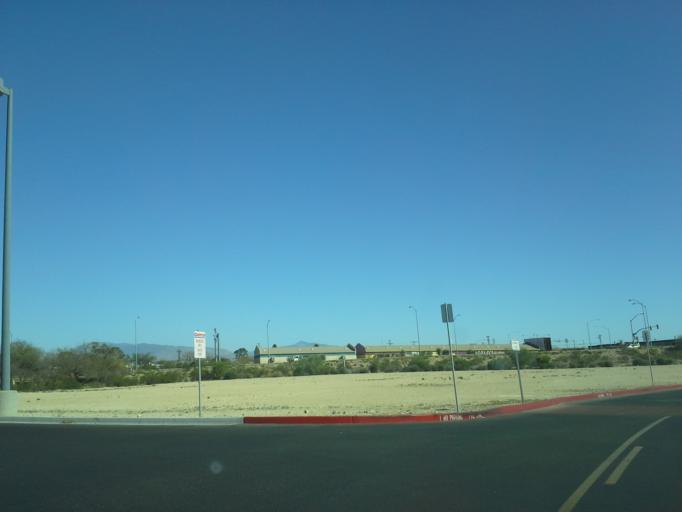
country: US
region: Arizona
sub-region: Pima County
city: South Tucson
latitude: 32.1817
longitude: -110.9463
